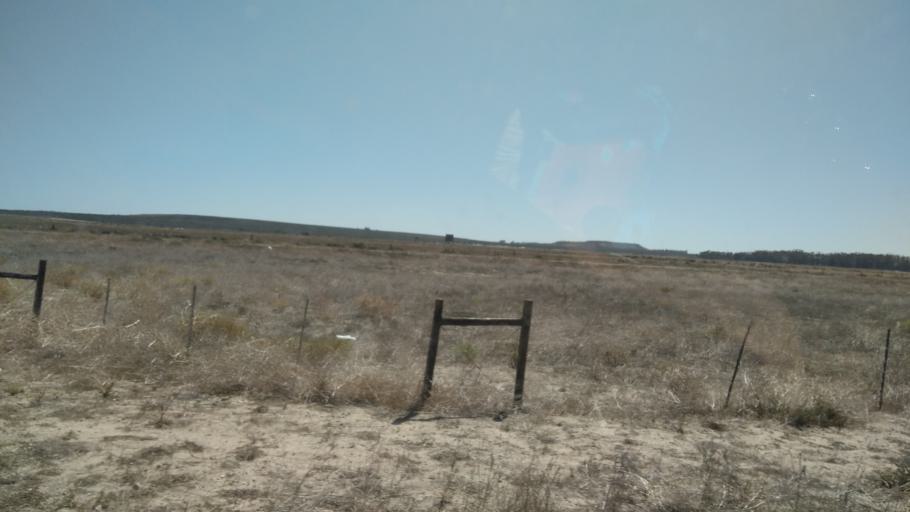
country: ZA
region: Western Cape
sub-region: West Coast District Municipality
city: Vredenburg
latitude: -32.9882
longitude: 18.1380
